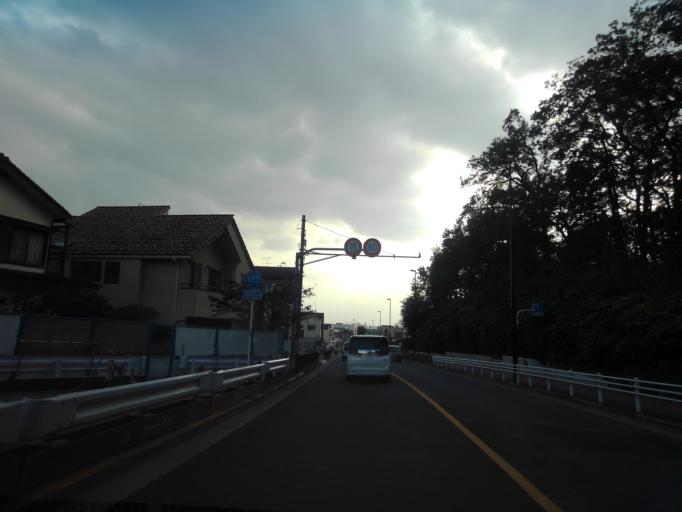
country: JP
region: Tokyo
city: Chofugaoka
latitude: 35.6728
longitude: 139.5389
